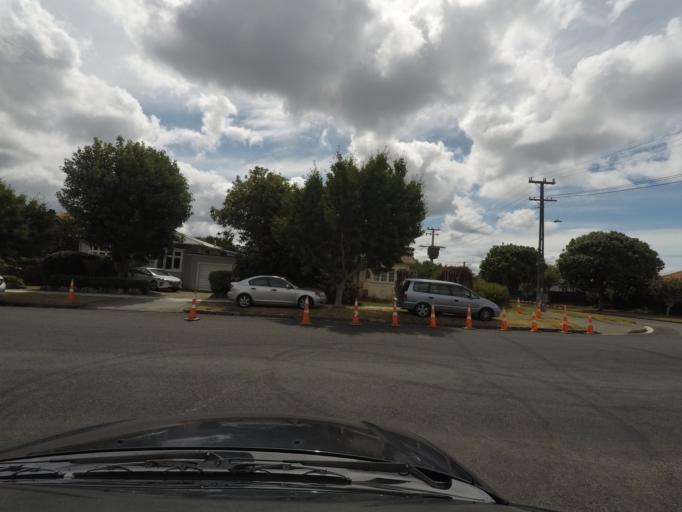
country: NZ
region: Auckland
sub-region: Auckland
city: Rosebank
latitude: -36.8858
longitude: 174.7061
